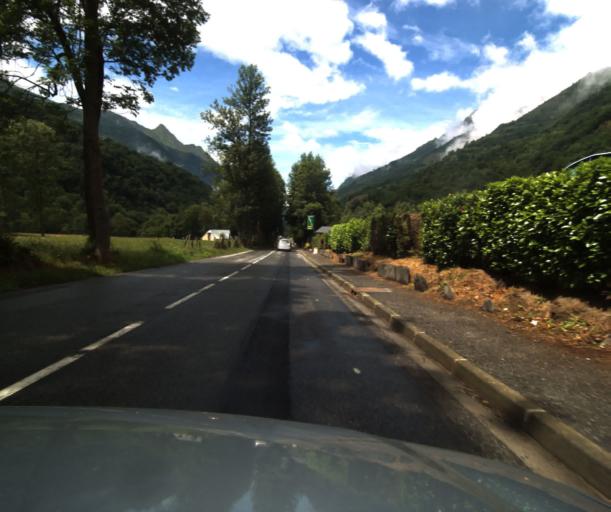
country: FR
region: Midi-Pyrenees
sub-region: Departement des Hautes-Pyrenees
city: Luz-Saint-Sauveur
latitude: 42.8823
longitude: -0.0132
